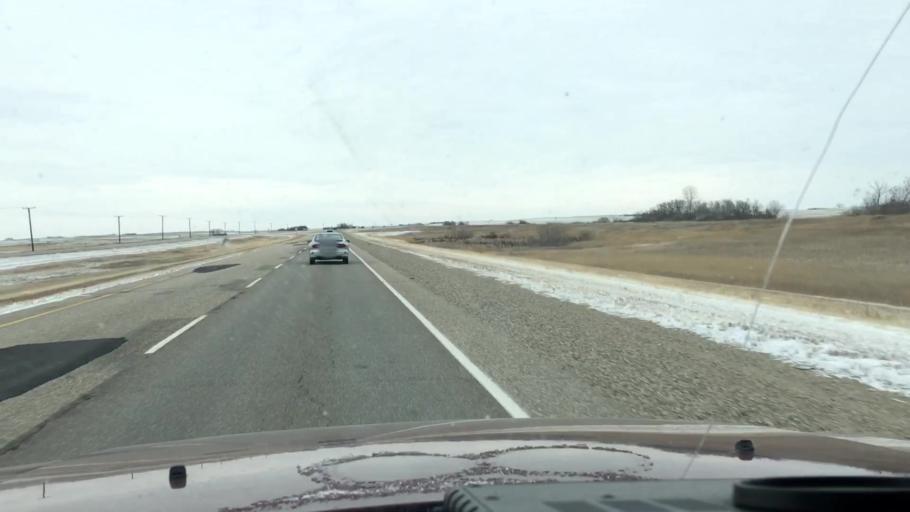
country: CA
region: Saskatchewan
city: Watrous
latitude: 51.4419
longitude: -106.2106
